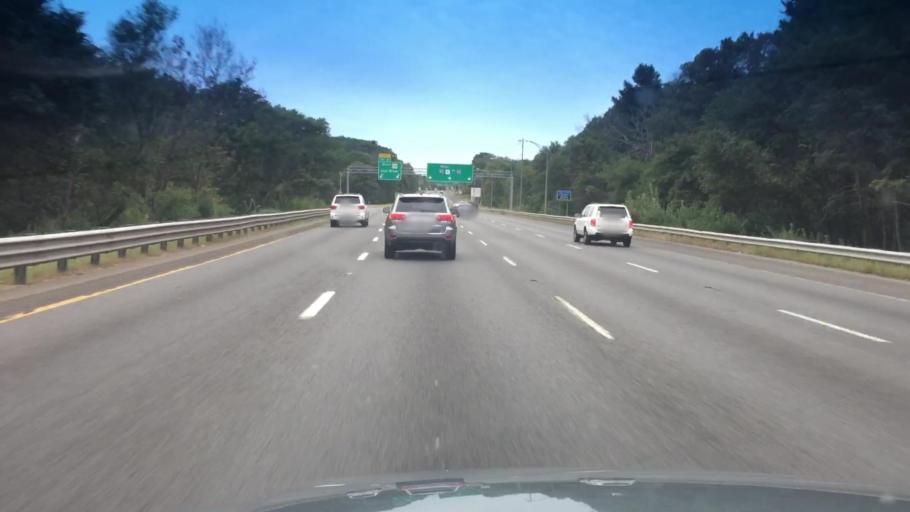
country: US
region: Massachusetts
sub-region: Norfolk County
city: Milton
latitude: 42.2049
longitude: -71.0726
